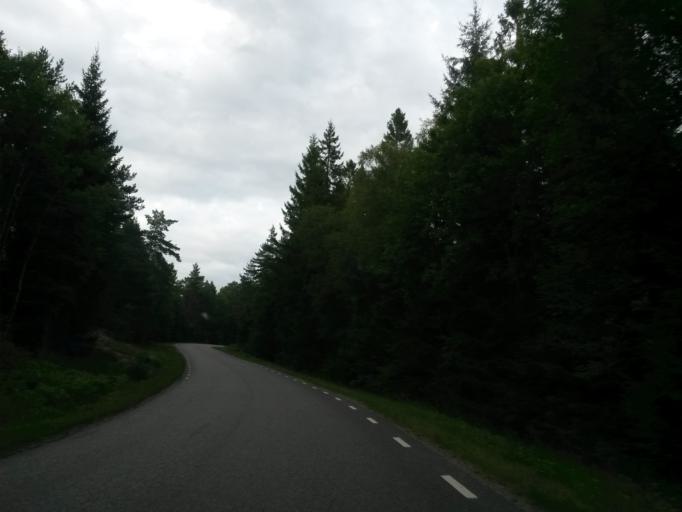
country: SE
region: Vaestra Goetaland
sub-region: Vargarda Kommun
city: Jonstorp
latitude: 57.9808
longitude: 12.6999
